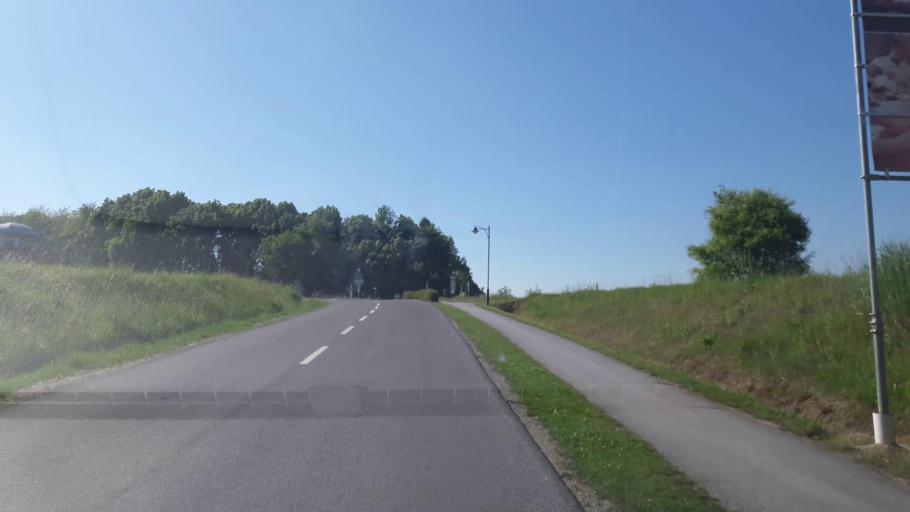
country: AT
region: Burgenland
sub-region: Politischer Bezirk Gussing
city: Stegersbach
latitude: 47.1716
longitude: 16.1474
